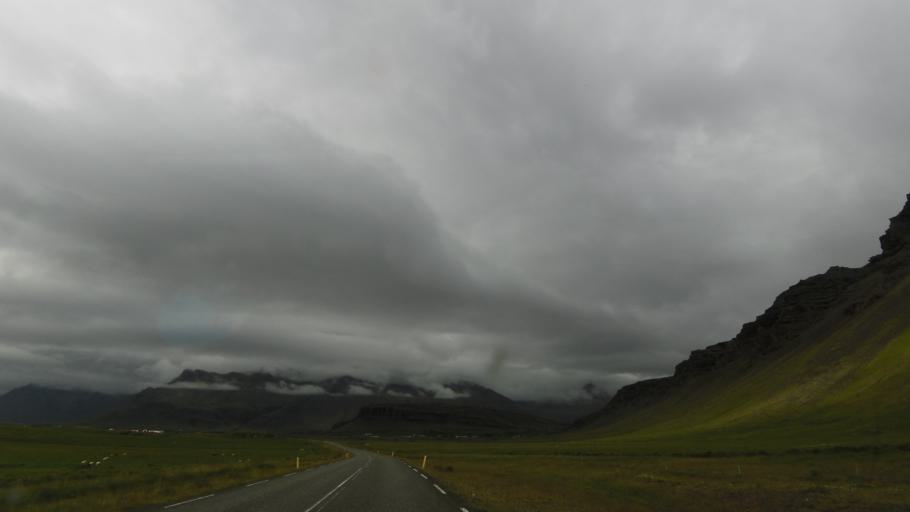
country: IS
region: East
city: Hoefn
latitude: 64.1808
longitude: -15.7833
